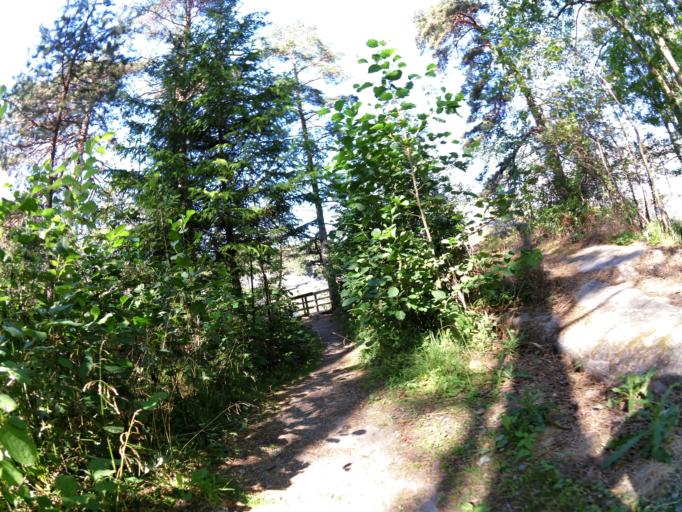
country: NO
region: Ostfold
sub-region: Fredrikstad
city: Fredrikstad
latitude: 59.1767
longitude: 10.8552
